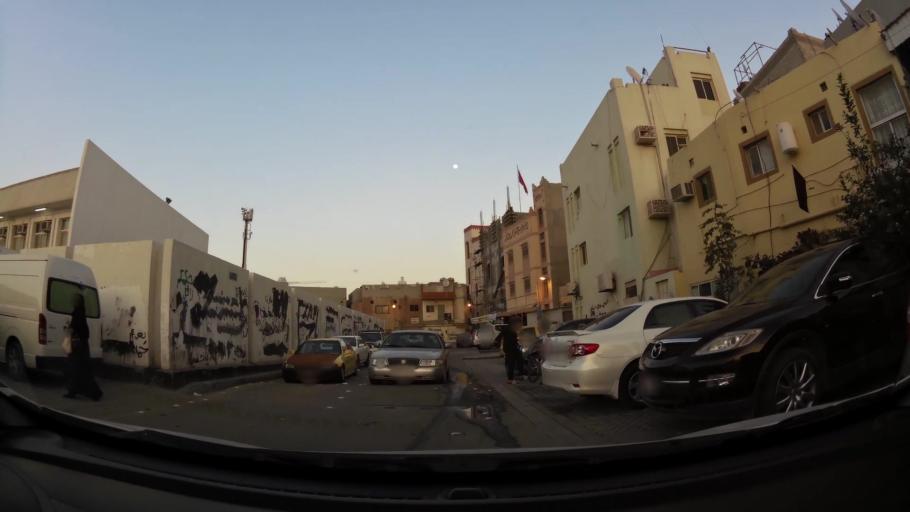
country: BH
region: Manama
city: Jidd Hafs
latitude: 26.2256
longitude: 50.5352
